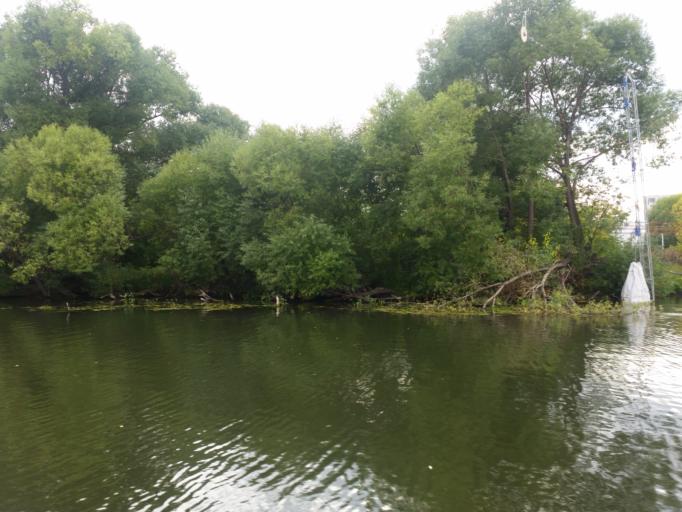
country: RU
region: Ulyanovsk
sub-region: Ulyanovskiy Rayon
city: Ulyanovsk
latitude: 54.3088
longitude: 48.3647
